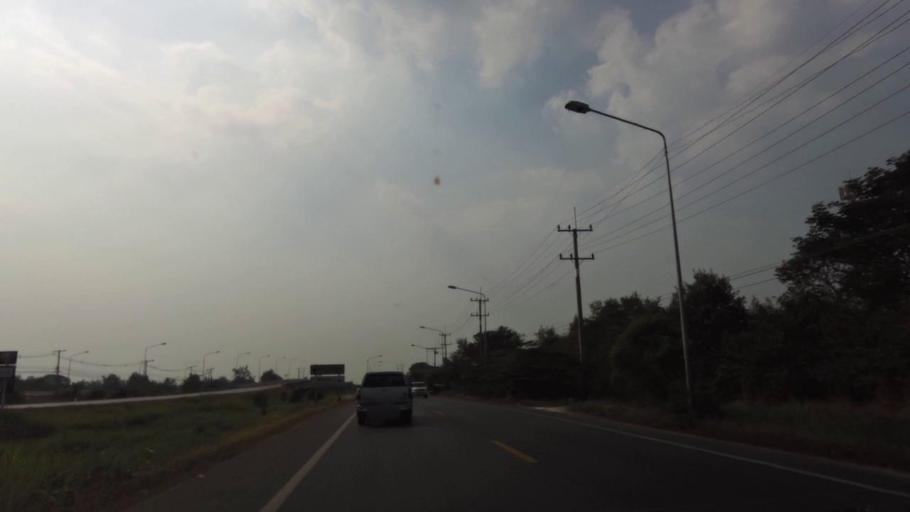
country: TH
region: Phra Nakhon Si Ayutthaya
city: Phra Nakhon Si Ayutthaya
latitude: 14.3046
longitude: 100.5717
